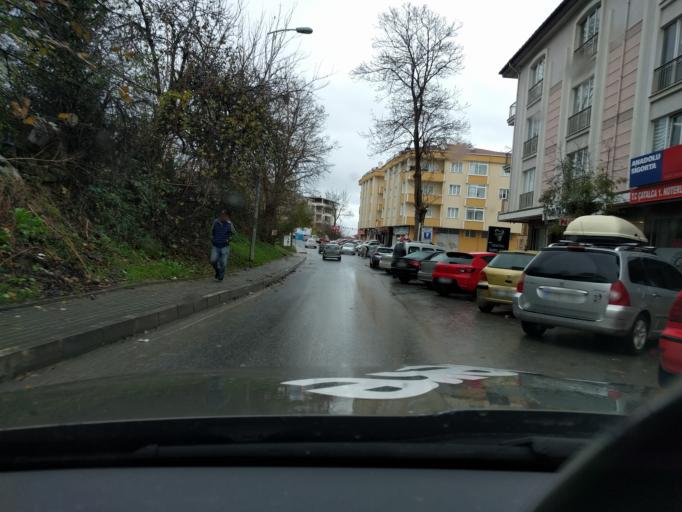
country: TR
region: Istanbul
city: Catalca
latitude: 41.1452
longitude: 28.4592
